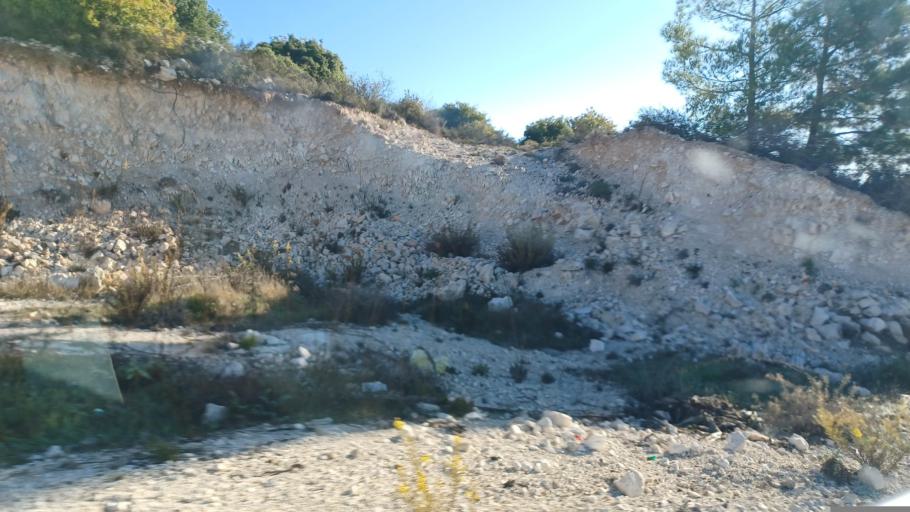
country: CY
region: Pafos
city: Polis
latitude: 34.9812
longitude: 32.5142
